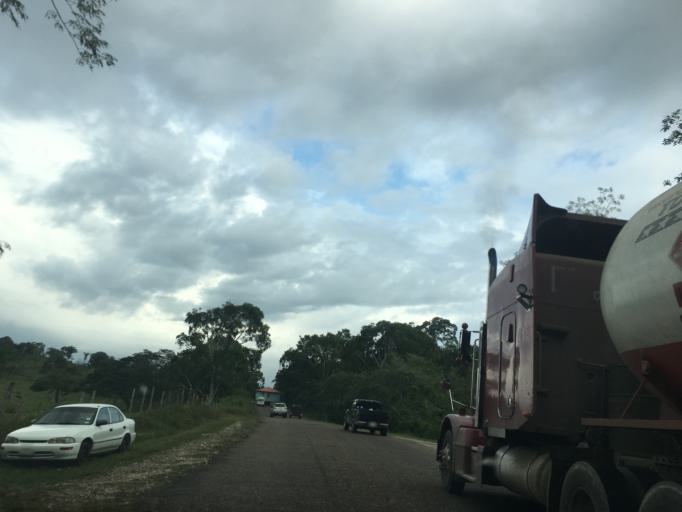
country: BZ
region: Cayo
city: San Ignacio
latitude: 17.2031
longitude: -88.9518
